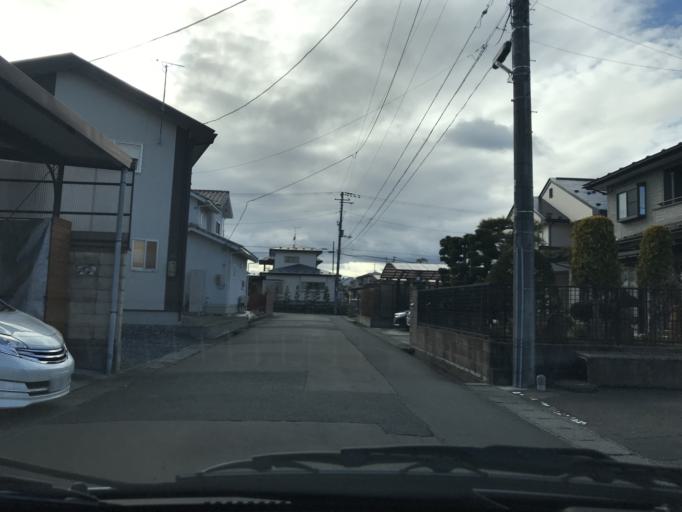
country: JP
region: Iwate
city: Mizusawa
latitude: 39.1145
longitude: 141.1419
